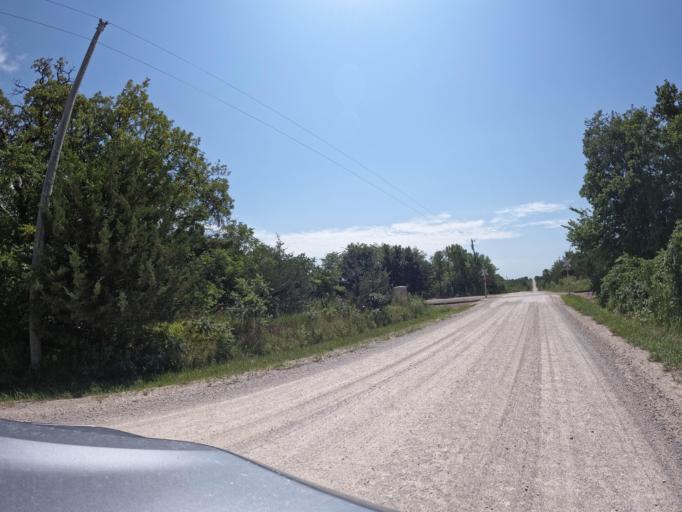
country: US
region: Iowa
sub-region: Appanoose County
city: Centerville
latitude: 40.7826
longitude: -92.9064
